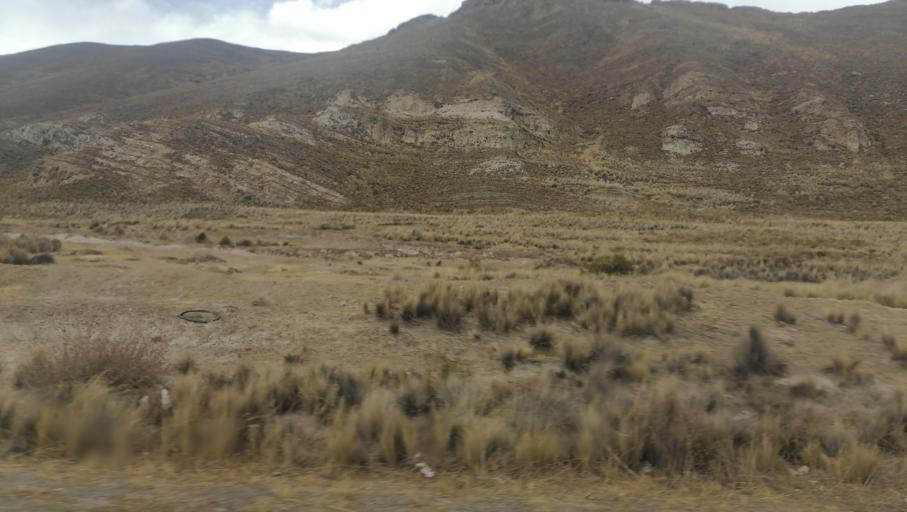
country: BO
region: Oruro
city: Totoral
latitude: -18.5863
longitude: -66.9298
